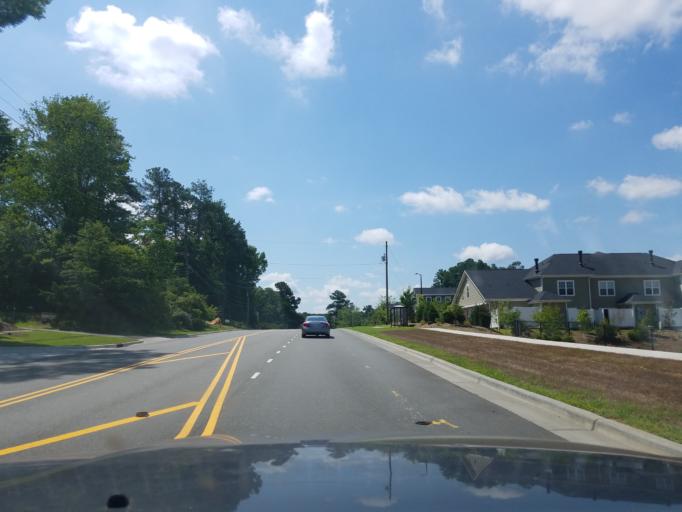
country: US
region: North Carolina
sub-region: Durham County
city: Durham
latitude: 35.9522
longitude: -78.9711
